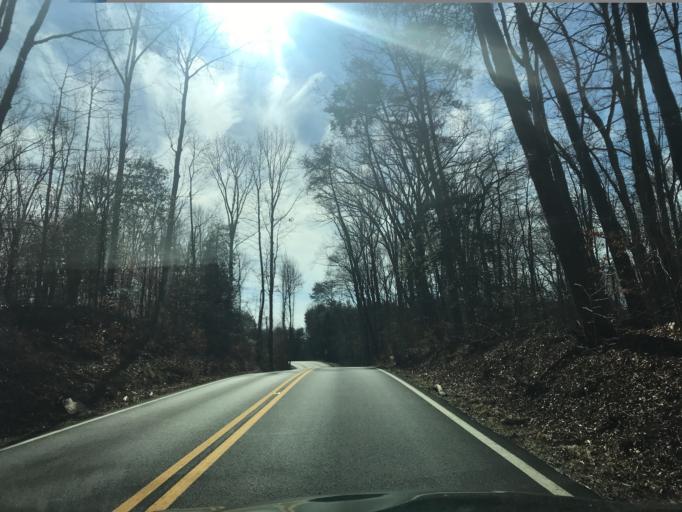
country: US
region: Maryland
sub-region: Charles County
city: Indian Head
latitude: 38.4953
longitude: -77.1584
